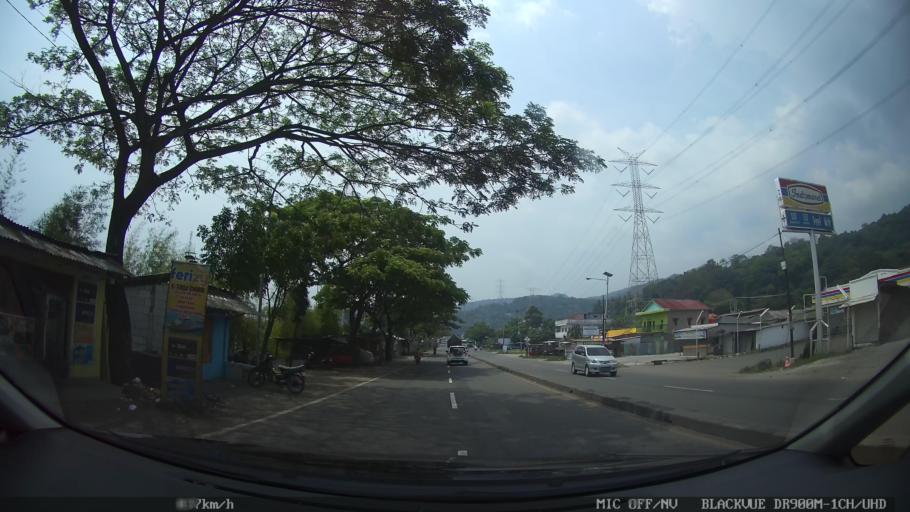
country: ID
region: Banten
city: Curug
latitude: -5.9661
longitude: 106.0057
